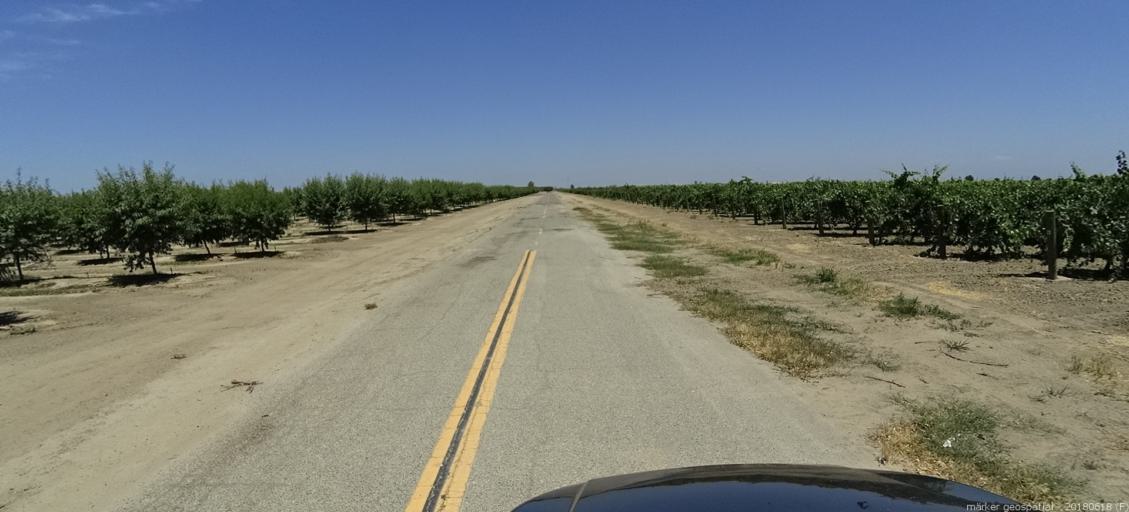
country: US
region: California
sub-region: Madera County
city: Parkwood
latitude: 36.9023
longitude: -120.1196
